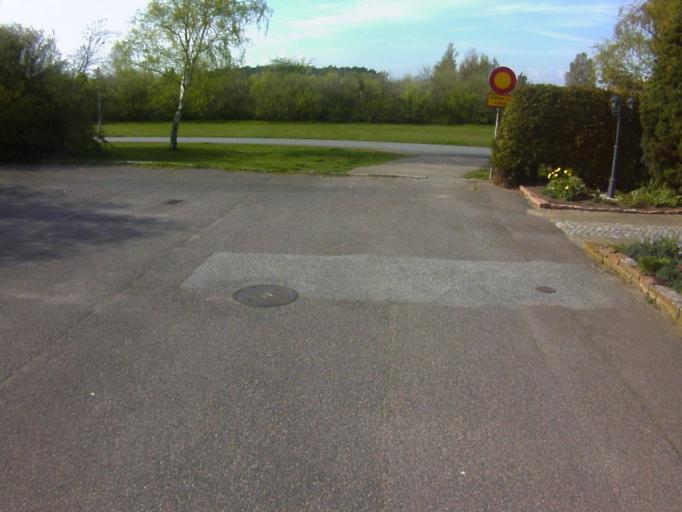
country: SE
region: Skane
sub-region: Kavlinge Kommun
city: Loddekopinge
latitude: 55.7625
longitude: 13.0139
